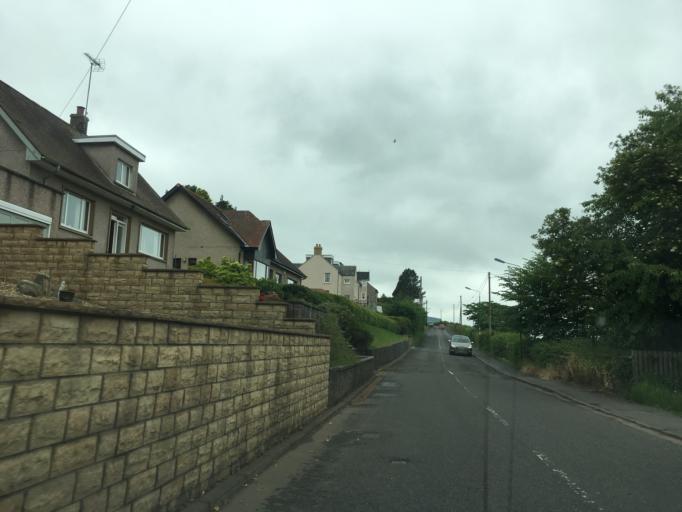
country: GB
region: Scotland
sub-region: Stirling
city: Stirling
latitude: 56.1093
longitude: -3.9711
